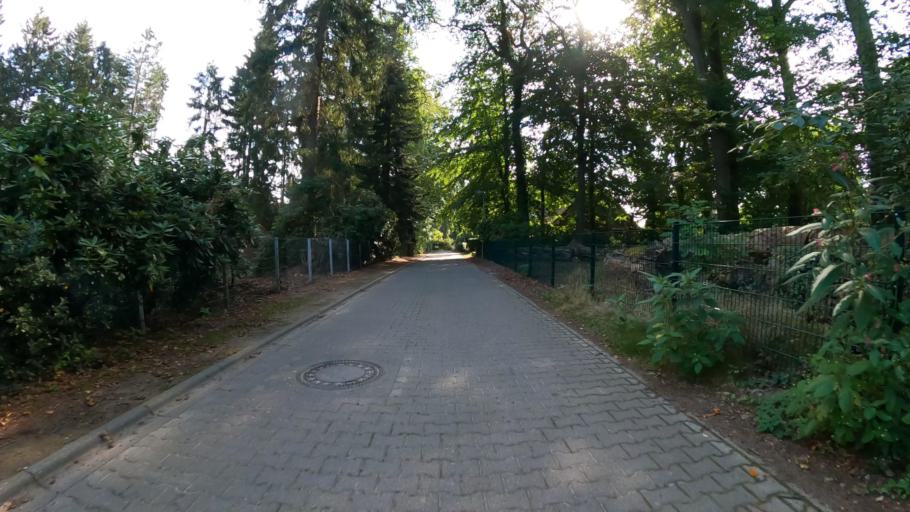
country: DE
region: Schleswig-Holstein
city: Kroppelshagen-Fahrendorf
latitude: 53.4945
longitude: 10.3484
